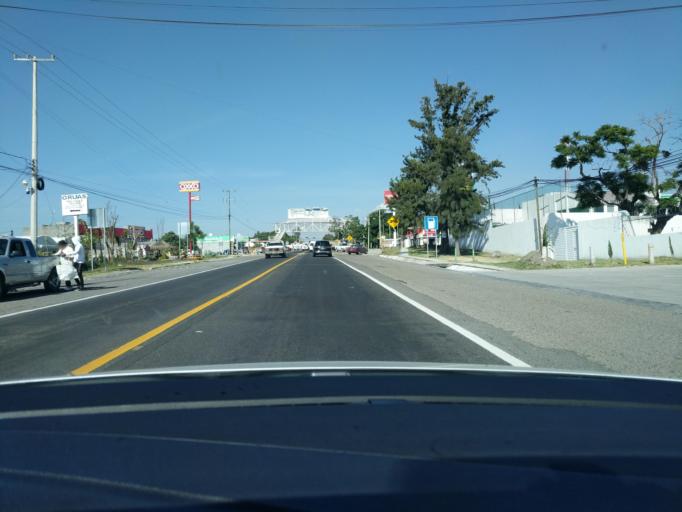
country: MX
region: Puebla
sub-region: Atlixco
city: San Agustin Huixaxtla
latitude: 18.9356
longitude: -98.4036
